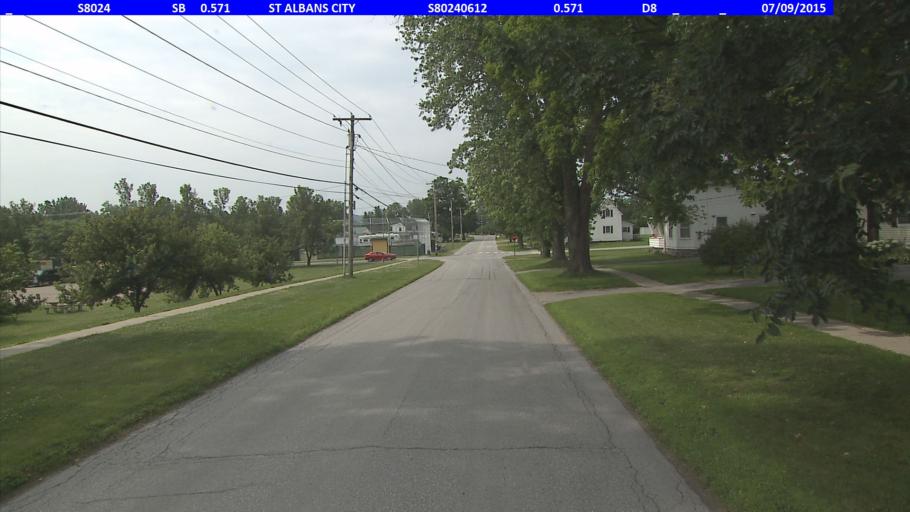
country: US
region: Vermont
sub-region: Franklin County
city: Saint Albans
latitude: 44.8191
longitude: -73.0899
